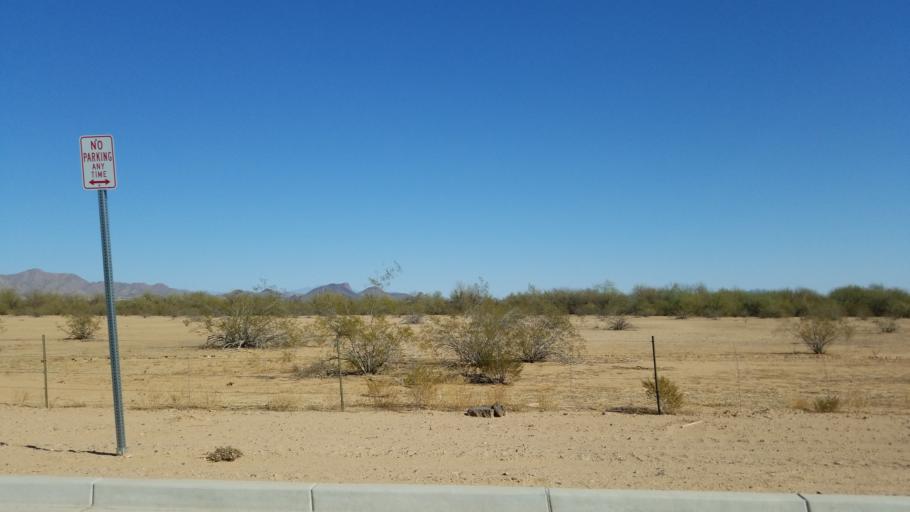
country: US
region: Arizona
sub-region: Maricopa County
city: Scottsdale
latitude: 33.5567
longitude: -111.8740
